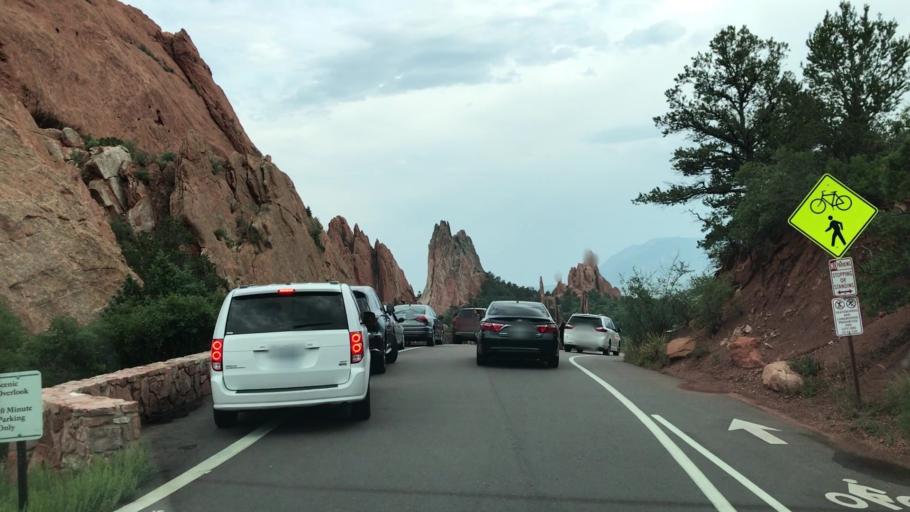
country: US
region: Colorado
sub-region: El Paso County
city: Manitou Springs
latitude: 38.8815
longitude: -104.8827
